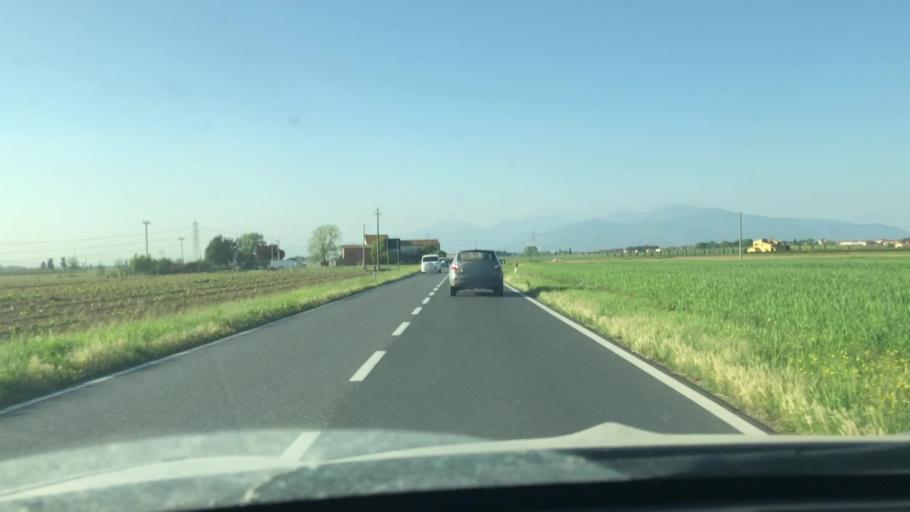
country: IT
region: Tuscany
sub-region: Province of Pisa
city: Cenaia
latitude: 43.5933
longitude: 10.5291
